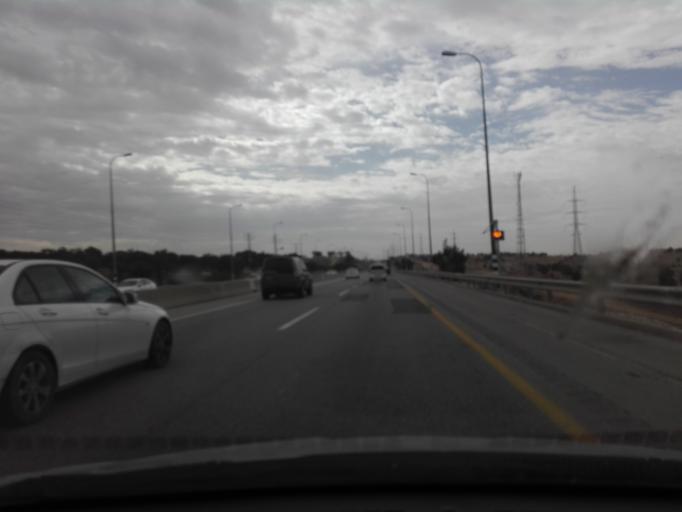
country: IL
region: Southern District
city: Lehavim
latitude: 31.3543
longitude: 34.7935
